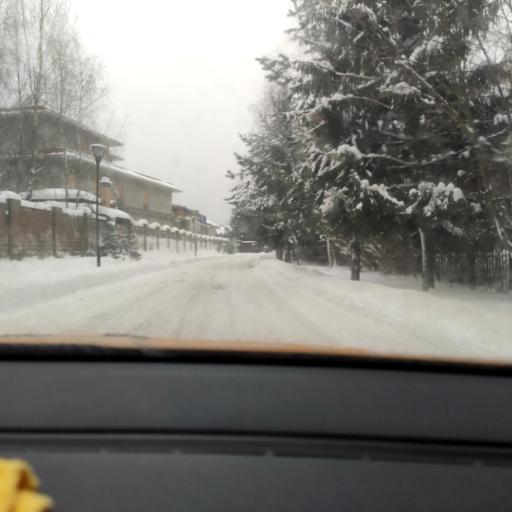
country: RU
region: Moskovskaya
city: Zarech'ye
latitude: 55.6771
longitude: 37.3939
